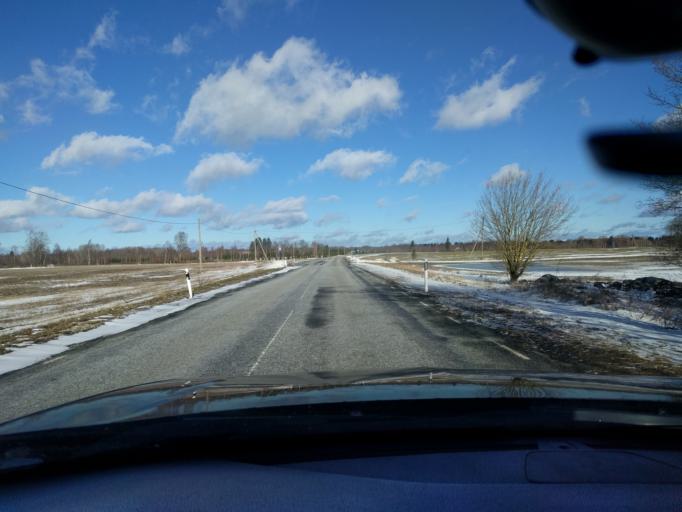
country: EE
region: Harju
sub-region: Raasiku vald
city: Raasiku
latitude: 59.3514
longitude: 25.1460
